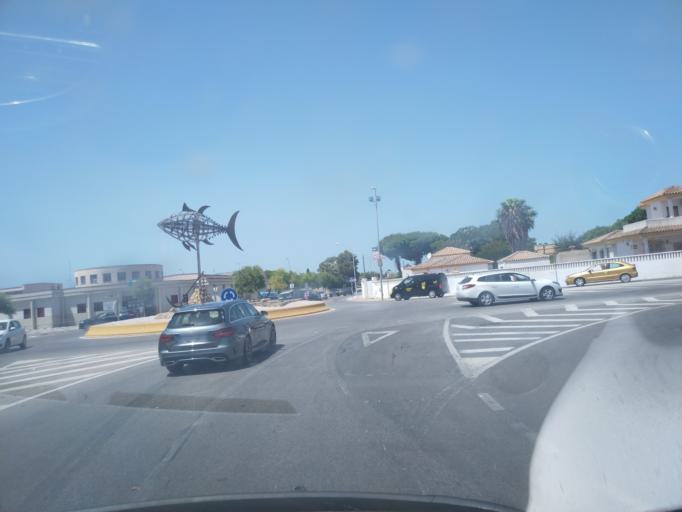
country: ES
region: Andalusia
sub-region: Provincia de Cadiz
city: Chiclana de la Frontera
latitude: 36.3960
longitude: -6.1679
